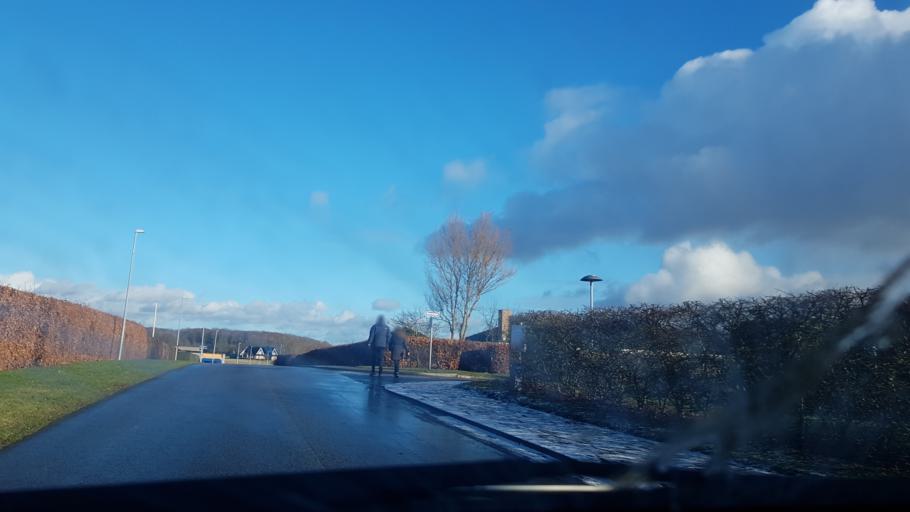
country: DK
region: South Denmark
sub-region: Fredericia Kommune
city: Taulov
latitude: 55.5186
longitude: 9.6408
